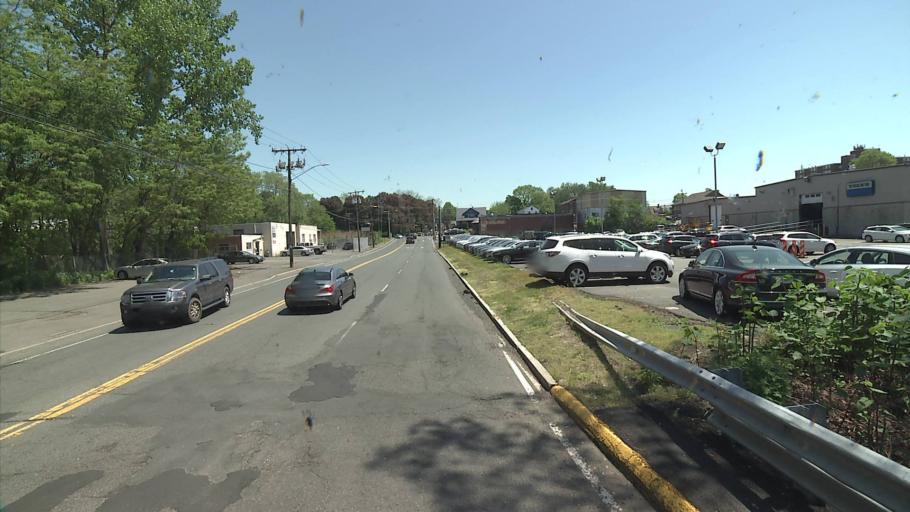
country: US
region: Connecticut
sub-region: Hartford County
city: Hartford
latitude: 41.7710
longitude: -72.6512
